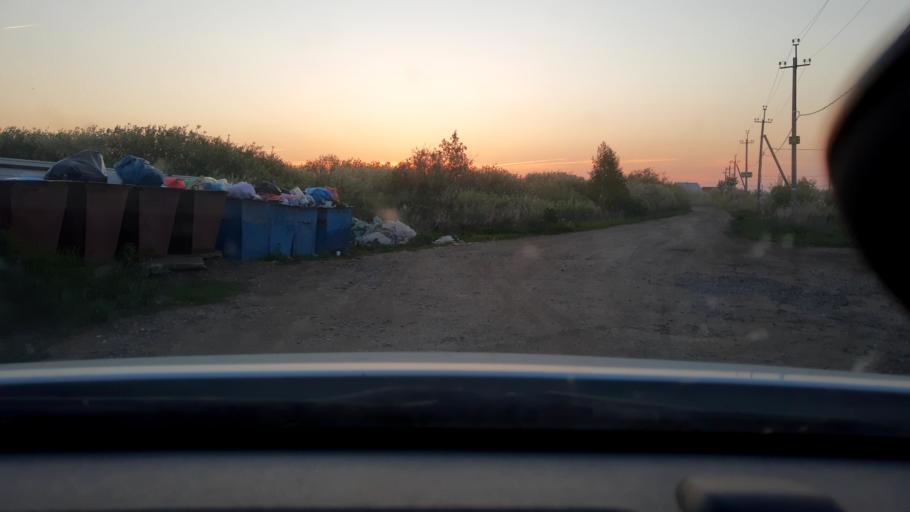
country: RU
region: Bashkortostan
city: Avdon
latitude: 54.5266
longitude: 55.8226
